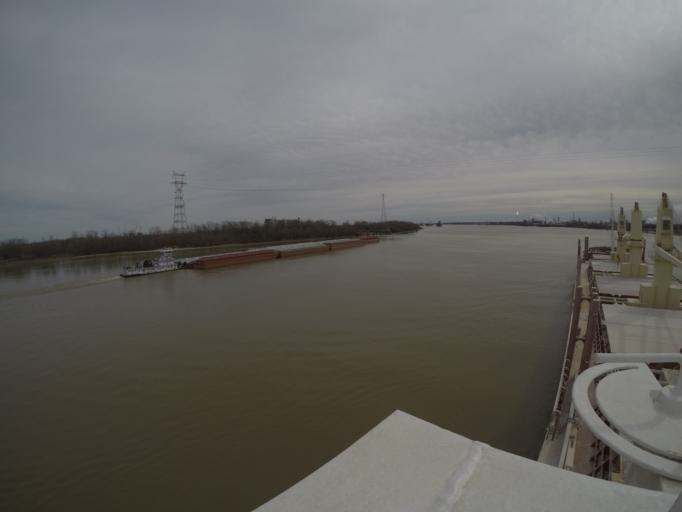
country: US
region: Louisiana
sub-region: Saint Charles Parish
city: Montz
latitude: 30.0025
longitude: -90.4723
